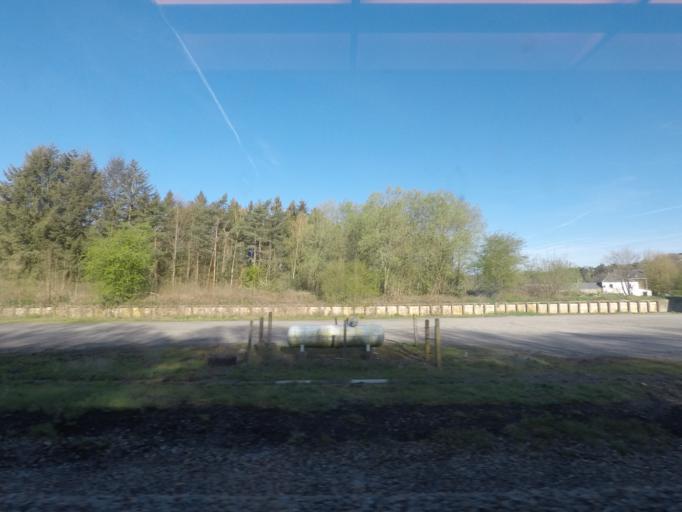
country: BE
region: Wallonia
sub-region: Province du Luxembourg
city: Tellin
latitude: 50.0900
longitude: 5.2798
